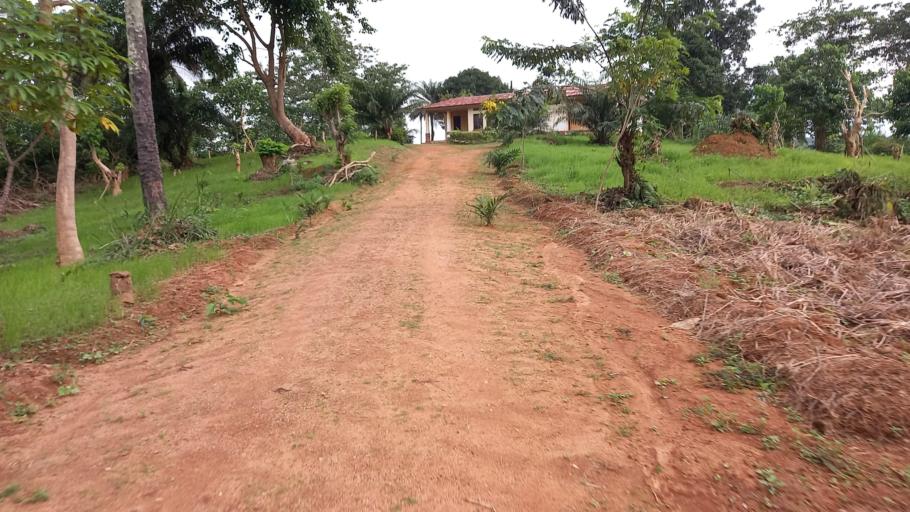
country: SL
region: Eastern Province
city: Kailahun
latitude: 8.2862
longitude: -10.5744
